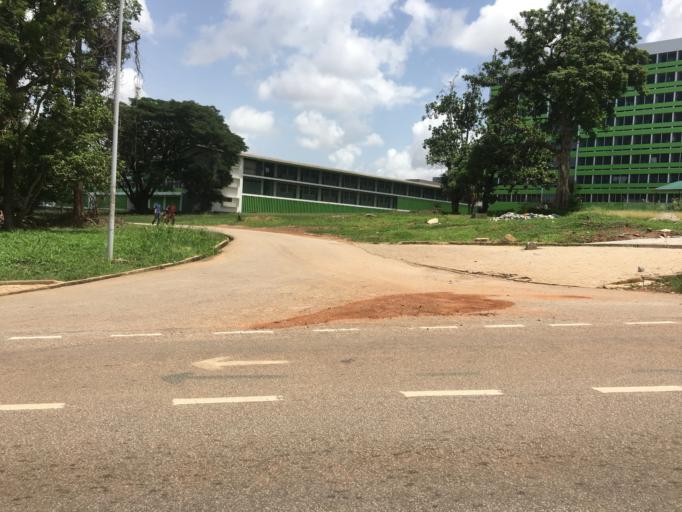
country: GH
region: Ashanti
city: Kumasi
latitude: 6.6791
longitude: -1.5725
